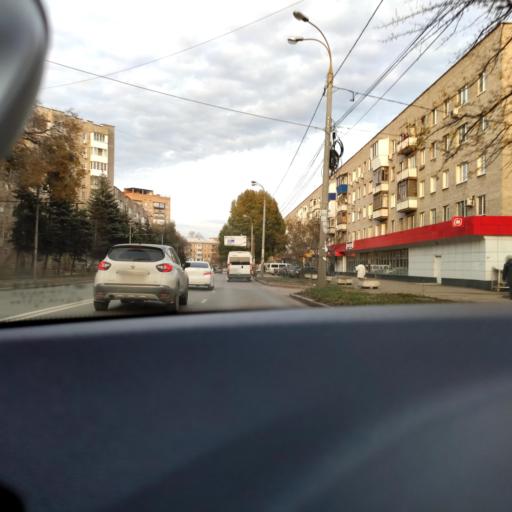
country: RU
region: Samara
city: Samara
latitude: 53.1999
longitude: 50.2255
